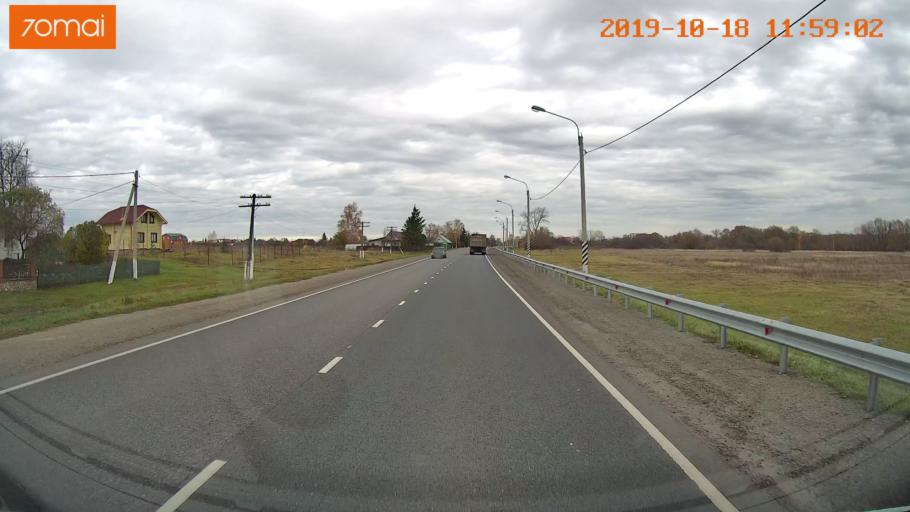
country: RU
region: Rjazan
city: Zakharovo
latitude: 54.2779
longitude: 39.1721
